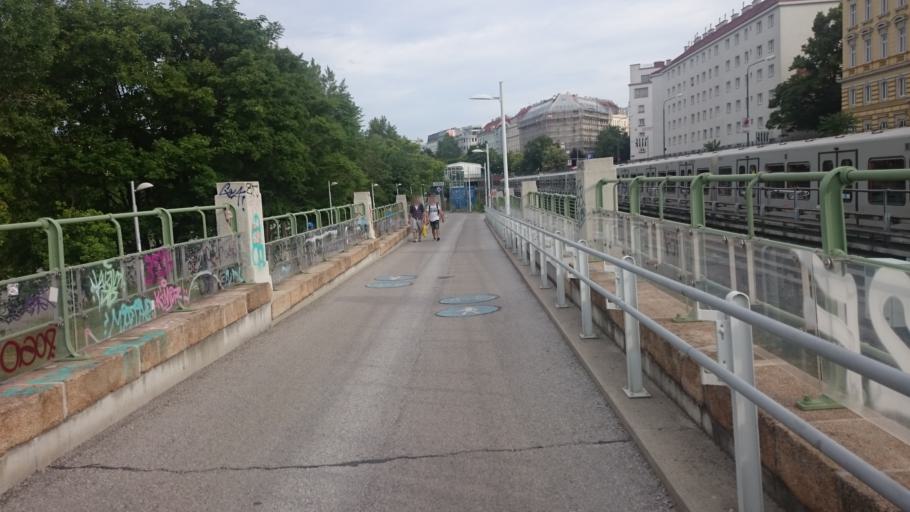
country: AT
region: Vienna
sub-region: Wien Stadt
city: Vienna
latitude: 48.2302
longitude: 16.3609
